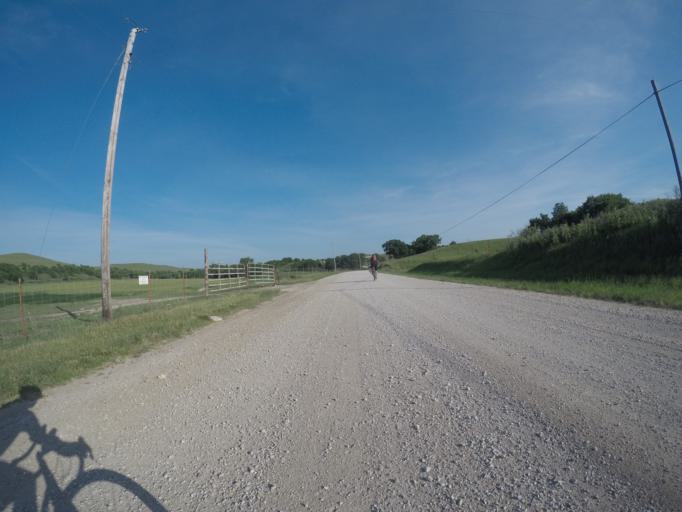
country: US
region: Kansas
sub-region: Riley County
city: Manhattan
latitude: 39.0605
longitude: -96.4988
